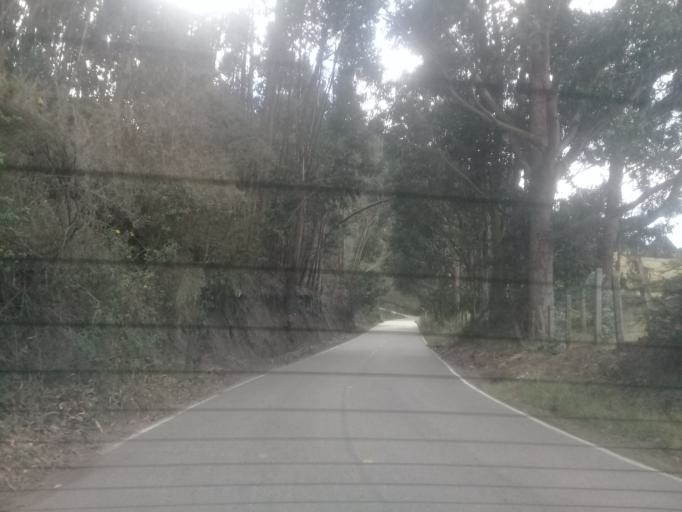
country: CO
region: Cundinamarca
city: Tabio
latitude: 4.9312
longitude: -74.1257
